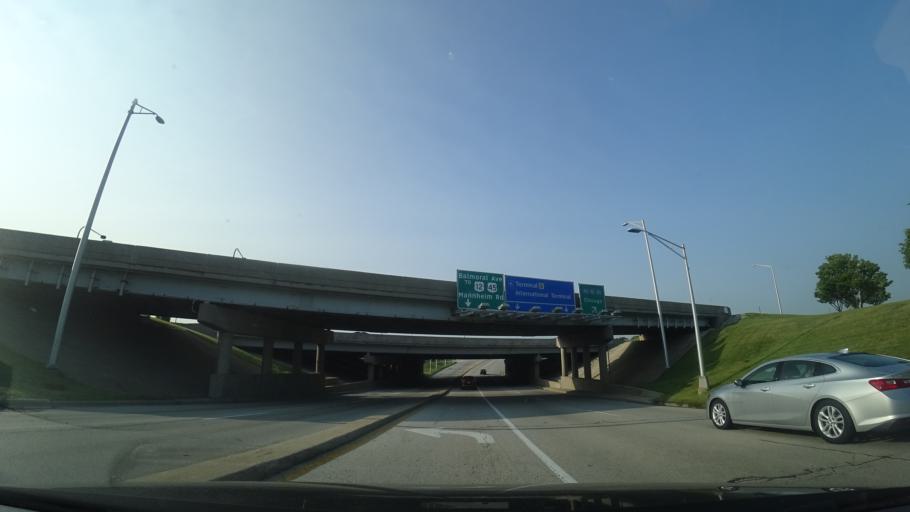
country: US
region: Illinois
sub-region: Cook County
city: Rosemont
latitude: 41.9790
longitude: -87.8856
